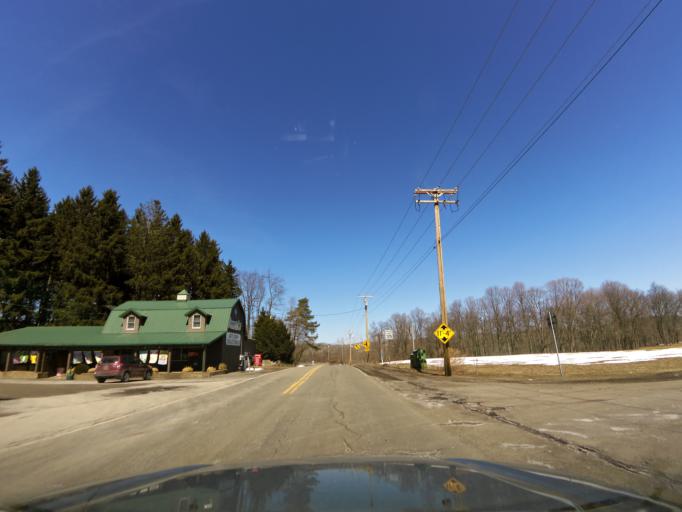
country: US
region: New York
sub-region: Cattaraugus County
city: Yorkshire
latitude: 42.5319
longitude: -78.4567
